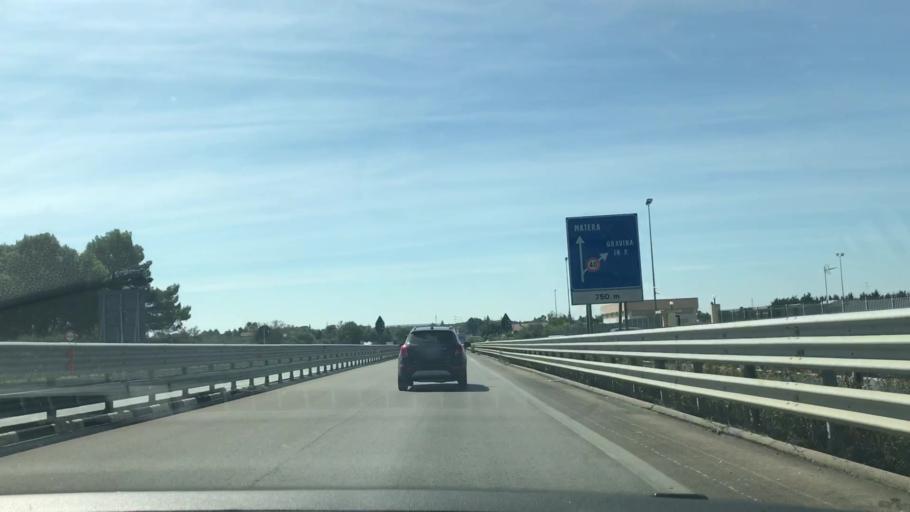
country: IT
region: Apulia
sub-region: Provincia di Bari
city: Altamura
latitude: 40.8025
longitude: 16.5548
